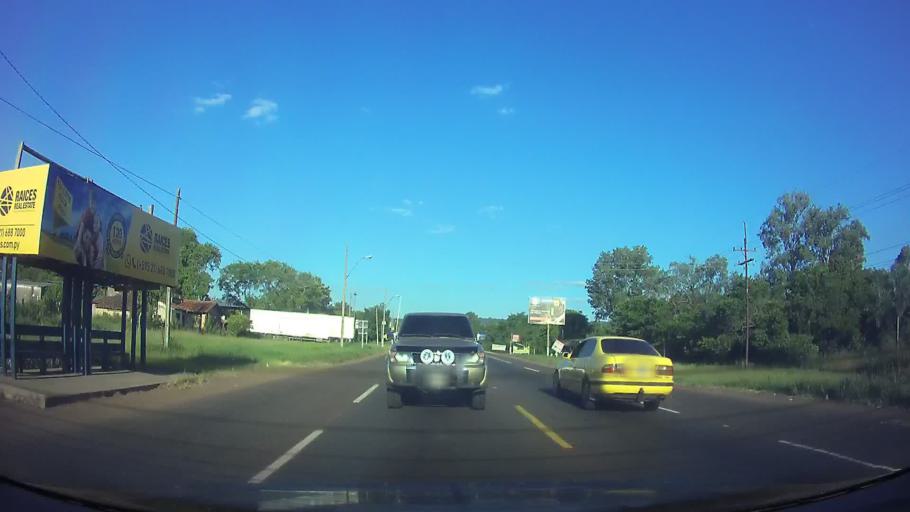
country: PY
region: Central
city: Ypacarai
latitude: -25.3813
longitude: -57.2523
